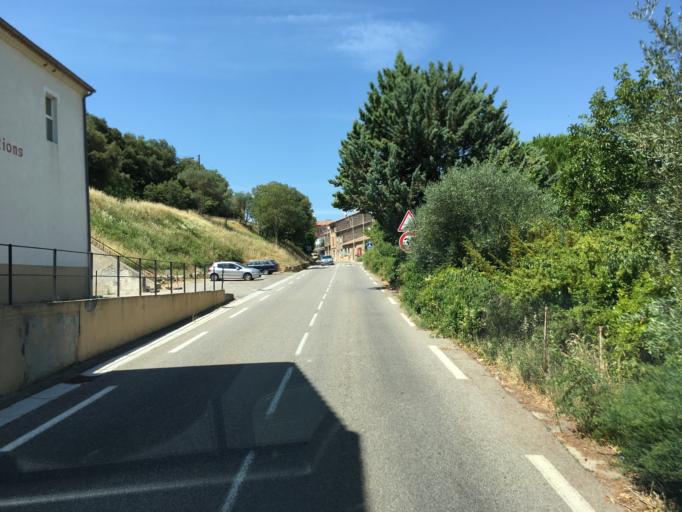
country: FR
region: Provence-Alpes-Cote d'Azur
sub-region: Departement du Var
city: Ginasservis
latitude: 43.6684
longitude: 5.8497
